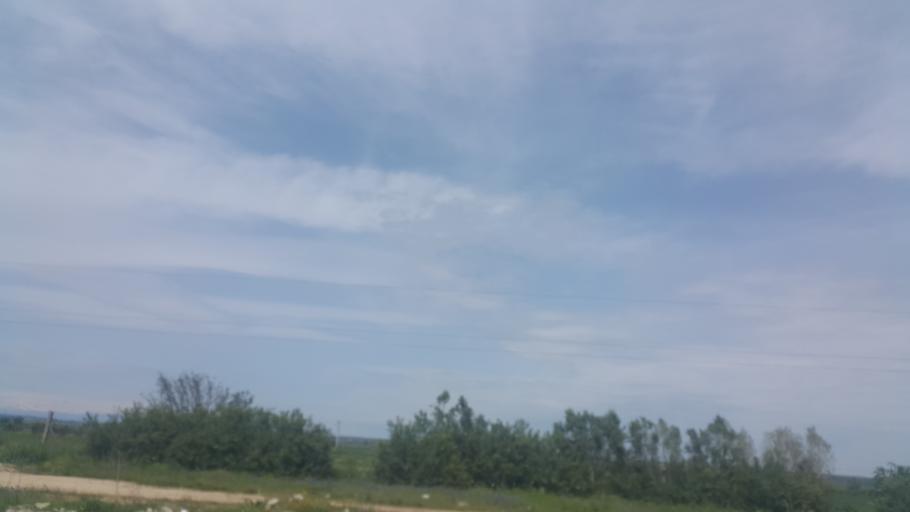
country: TR
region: Adana
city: Yuregir
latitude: 36.9770
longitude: 35.4762
